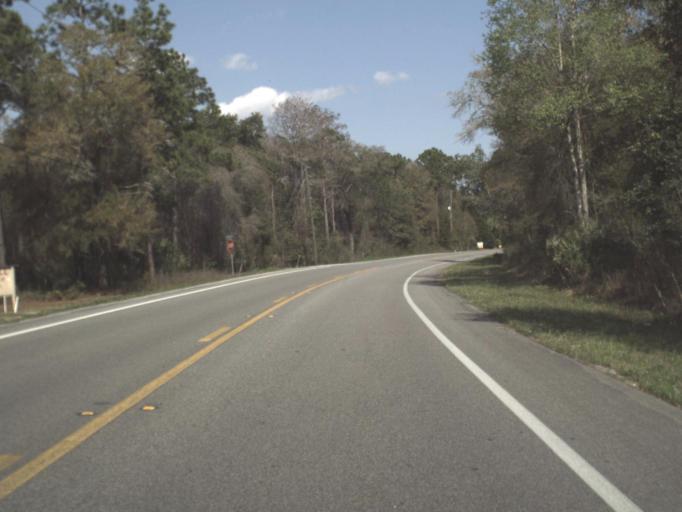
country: US
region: Florida
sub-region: Wakulla County
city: Crawfordville
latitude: 30.0753
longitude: -84.4317
